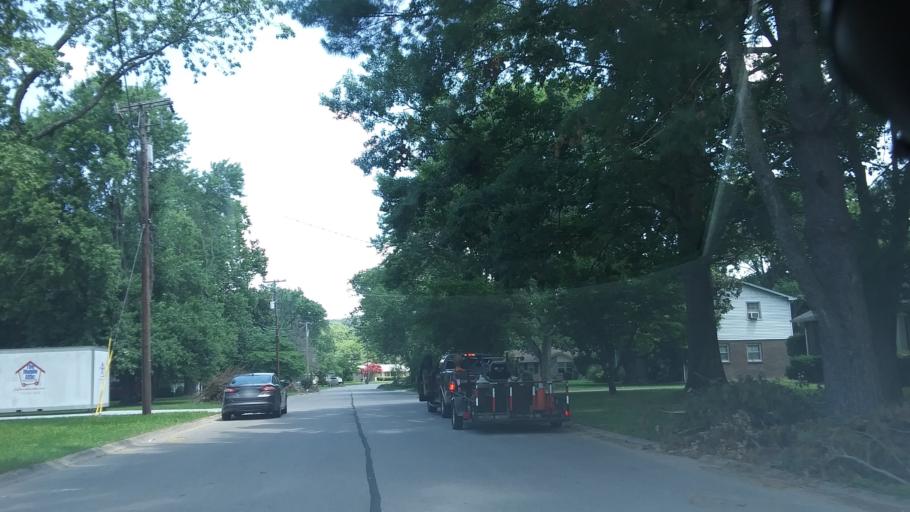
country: US
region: Tennessee
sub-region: Davidson County
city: Belle Meade
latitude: 36.0821
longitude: -86.9428
